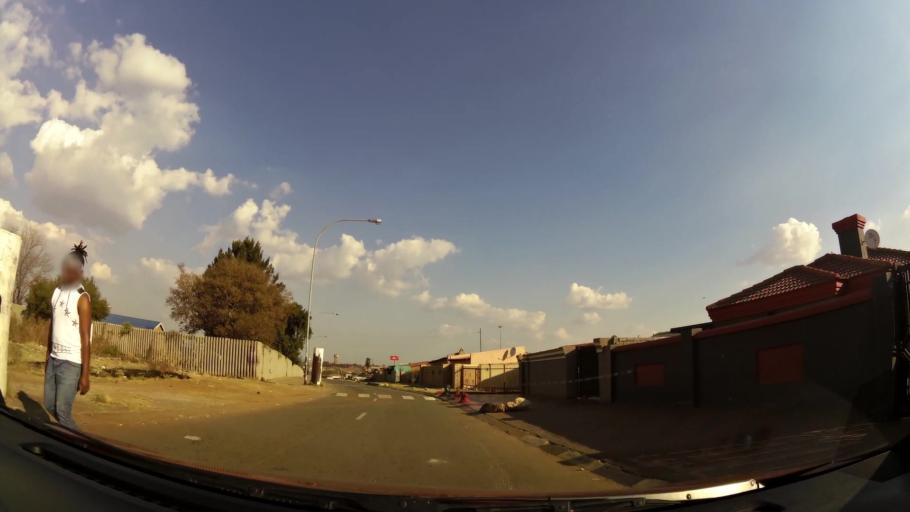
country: ZA
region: Gauteng
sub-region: City of Johannesburg Metropolitan Municipality
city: Soweto
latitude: -26.2319
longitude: 27.8598
